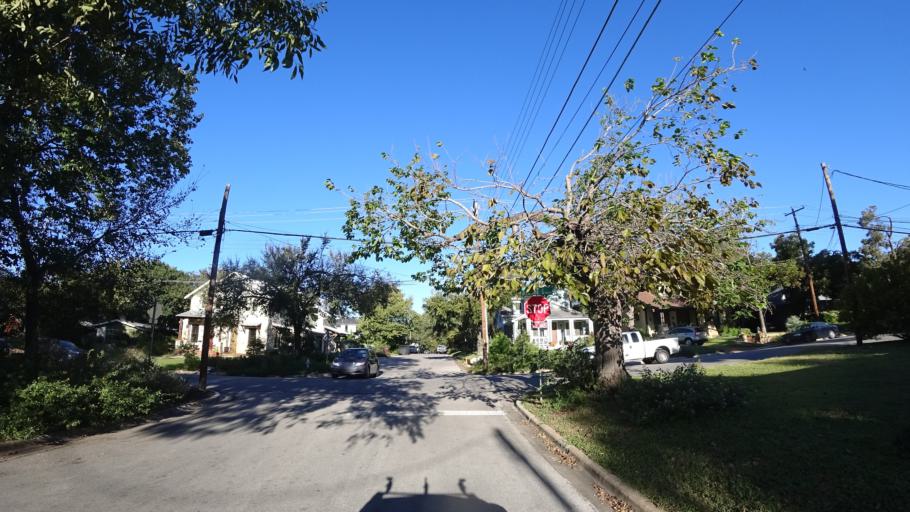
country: US
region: Texas
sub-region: Travis County
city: Austin
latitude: 30.3096
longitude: -97.7250
